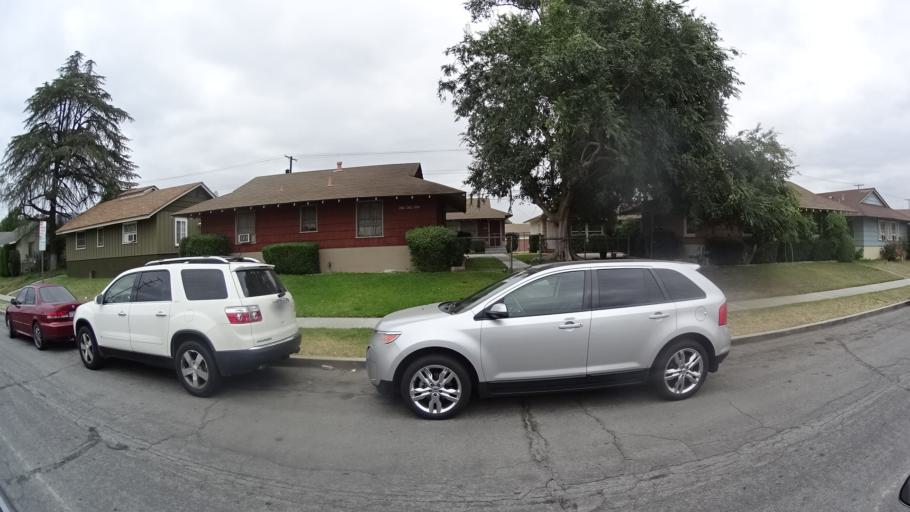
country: US
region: California
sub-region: Los Angeles County
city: Burbank
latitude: 34.1899
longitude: -118.3446
